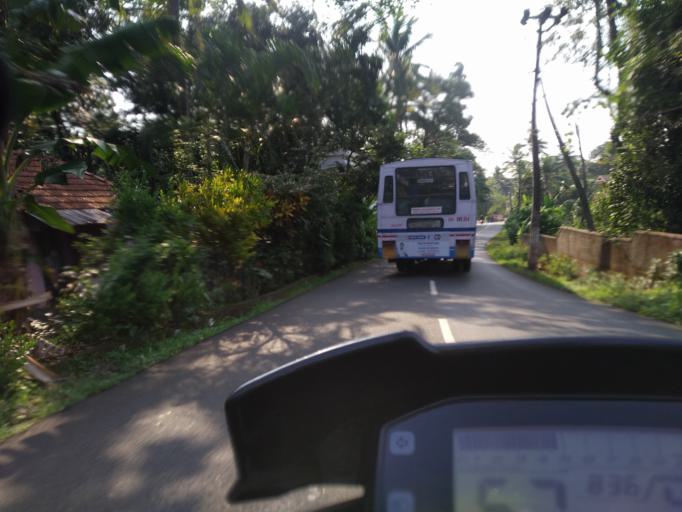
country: IN
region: Kerala
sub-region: Ernakulam
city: Ramamangalam
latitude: 9.9145
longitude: 76.4298
